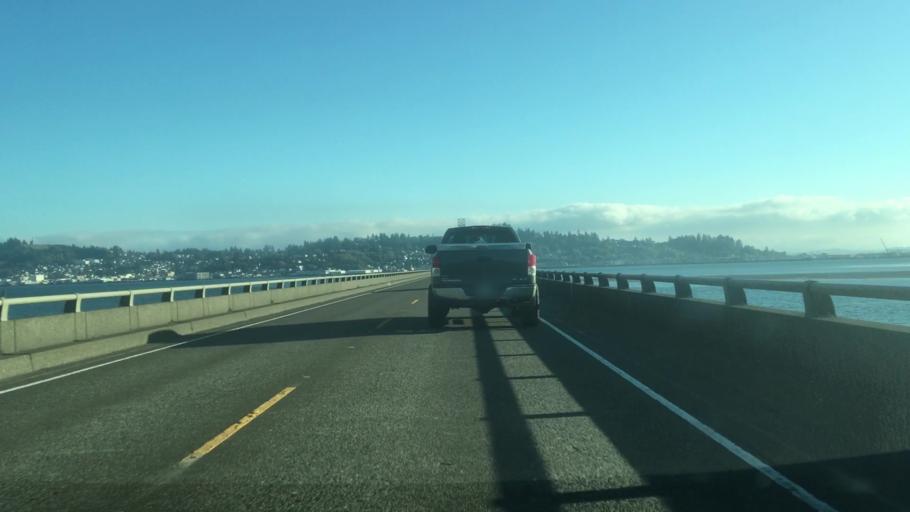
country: US
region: Oregon
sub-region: Clatsop County
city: Astoria
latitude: 46.2108
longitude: -123.8597
